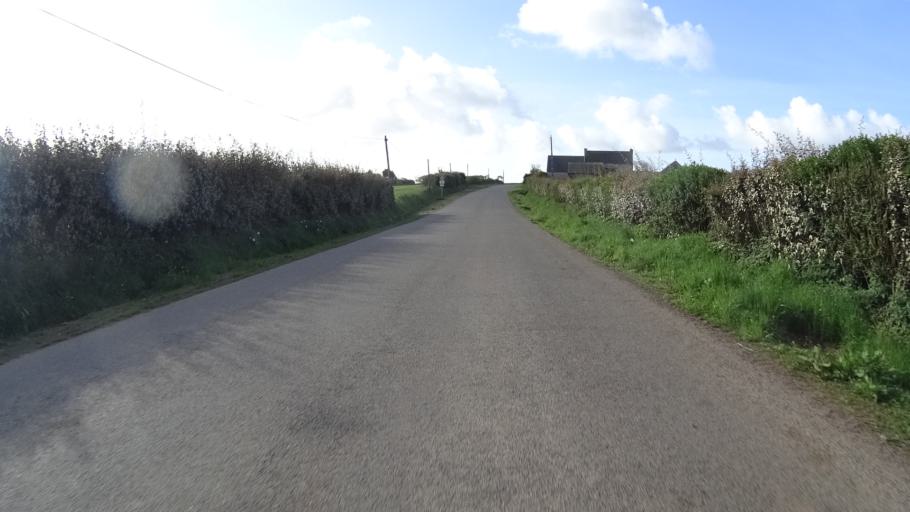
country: FR
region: Brittany
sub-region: Departement du Finistere
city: Plouzane
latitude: 48.3925
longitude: -4.6629
